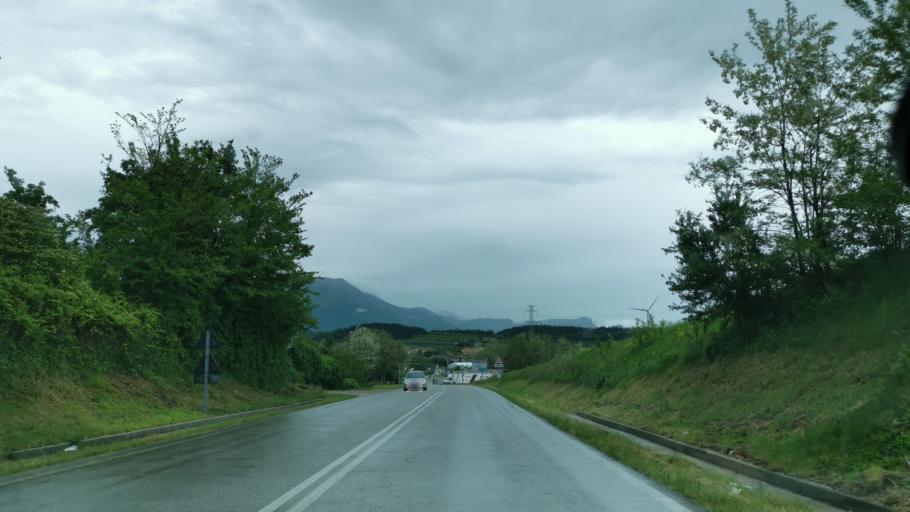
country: IT
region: Veneto
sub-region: Provincia di Verona
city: Affi
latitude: 45.5485
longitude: 10.7779
